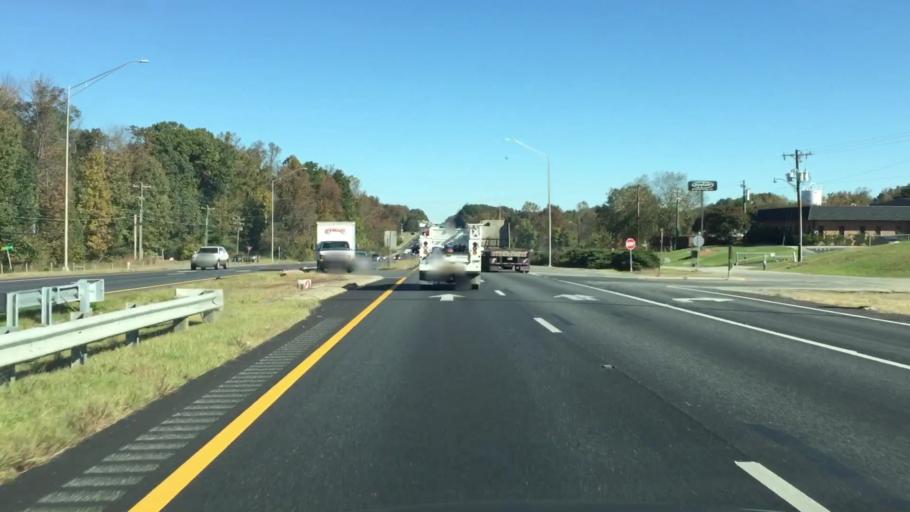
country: US
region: North Carolina
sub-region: Guilford County
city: Greensboro
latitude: 36.1214
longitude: -79.7509
